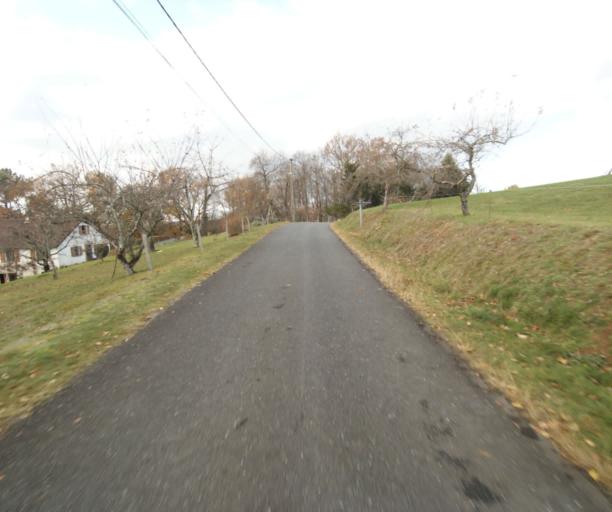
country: FR
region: Limousin
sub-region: Departement de la Correze
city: Laguenne
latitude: 45.2271
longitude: 1.7916
